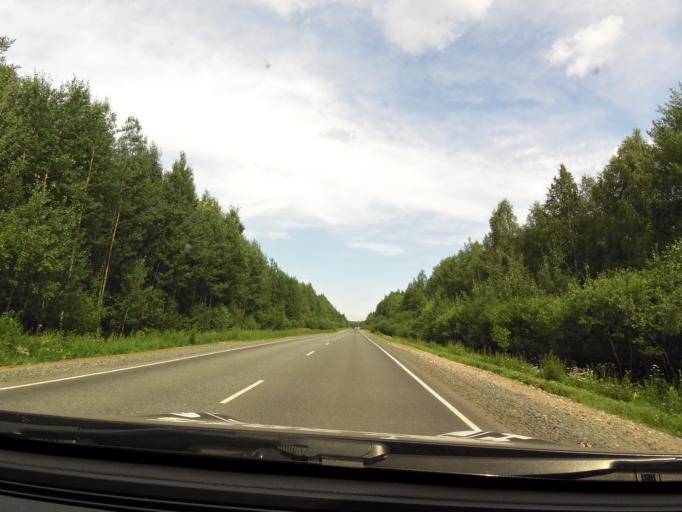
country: RU
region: Kirov
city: Slobodskoy
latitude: 58.7266
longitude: 50.2262
